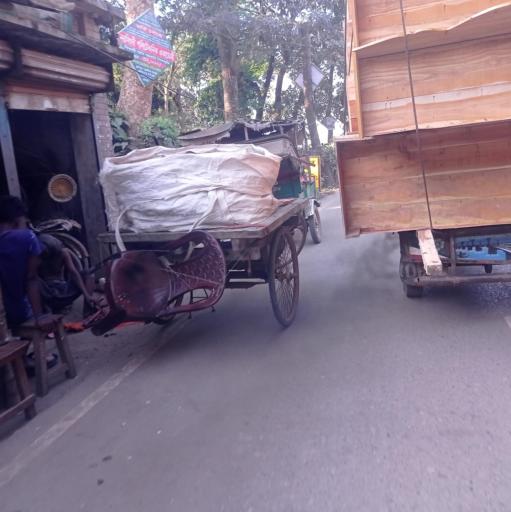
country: BD
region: Dhaka
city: Bhairab Bazar
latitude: 24.1088
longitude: 90.8505
